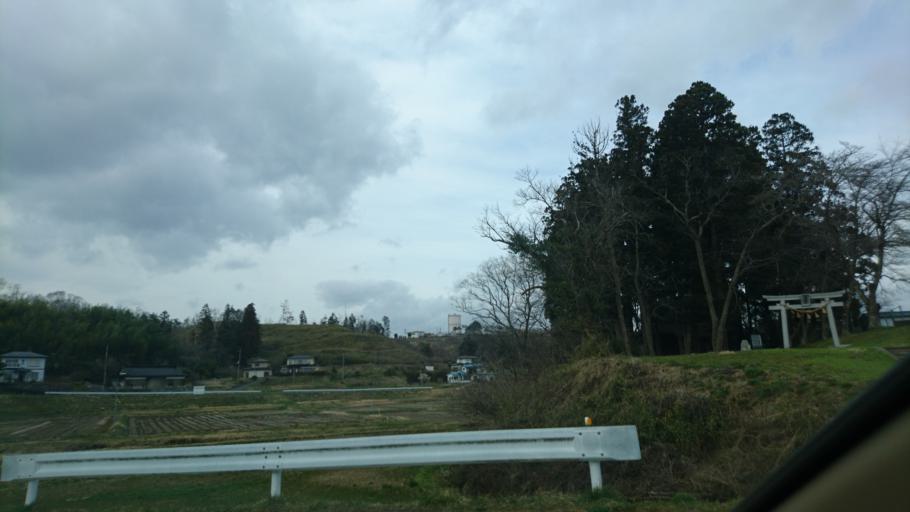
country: JP
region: Iwate
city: Ichinoseki
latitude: 38.8989
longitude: 141.1603
